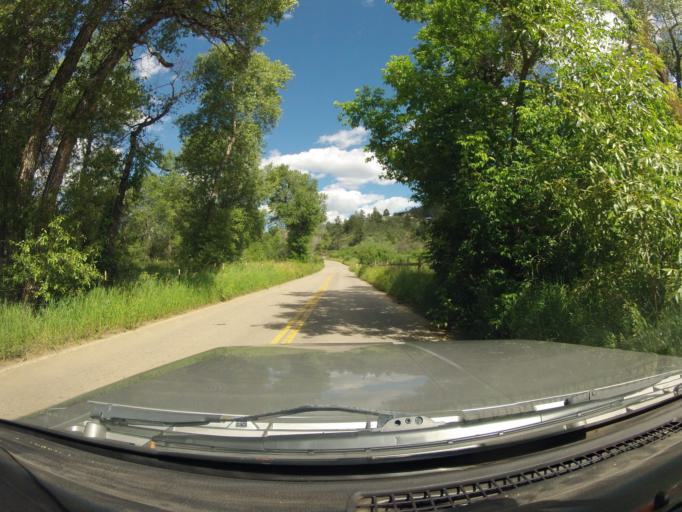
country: US
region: Colorado
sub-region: Larimer County
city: Laporte
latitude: 40.5674
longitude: -105.3136
